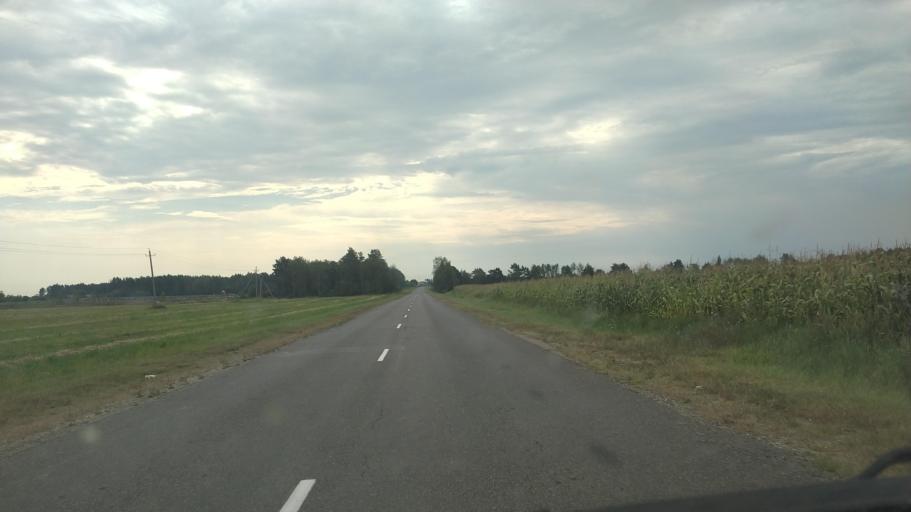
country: BY
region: Brest
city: Byaroza
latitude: 52.5633
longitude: 24.9045
